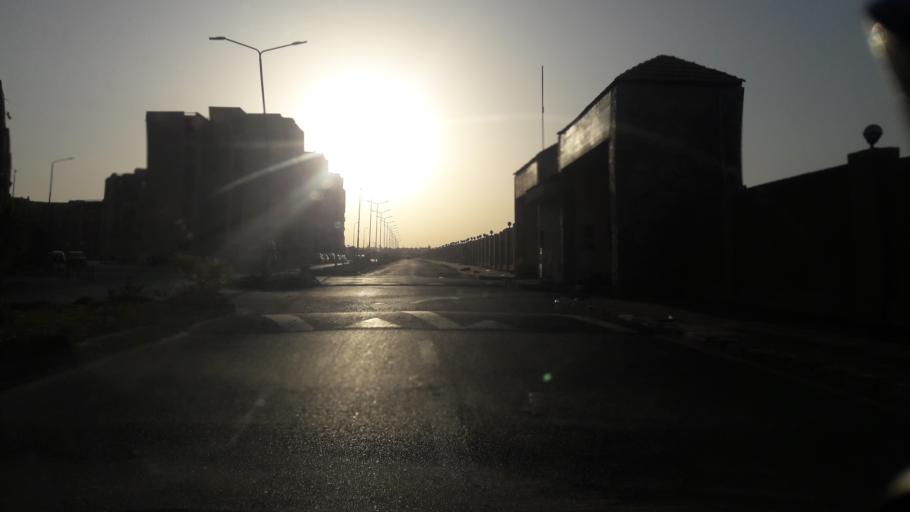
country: EG
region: Al Jizah
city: Madinat Sittah Uktubar
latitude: 29.9589
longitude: 31.0416
